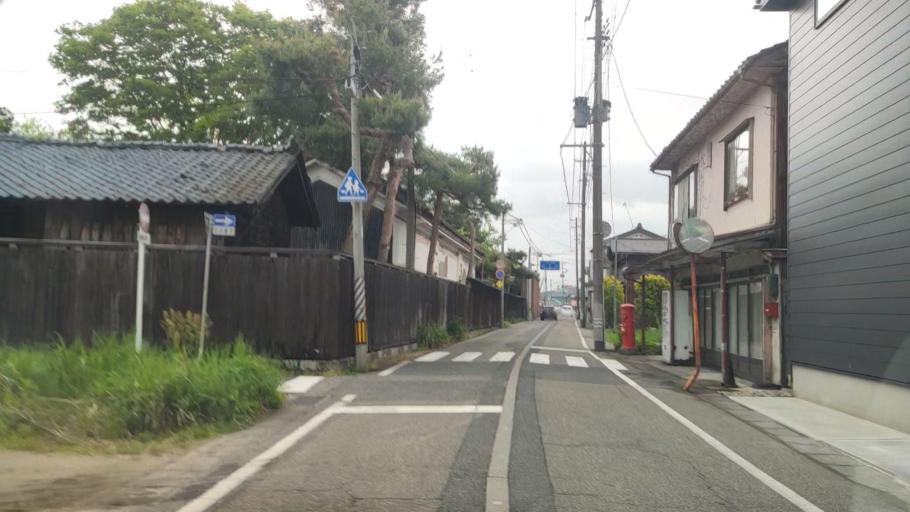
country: JP
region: Niigata
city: Gosen
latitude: 37.7376
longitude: 139.1749
